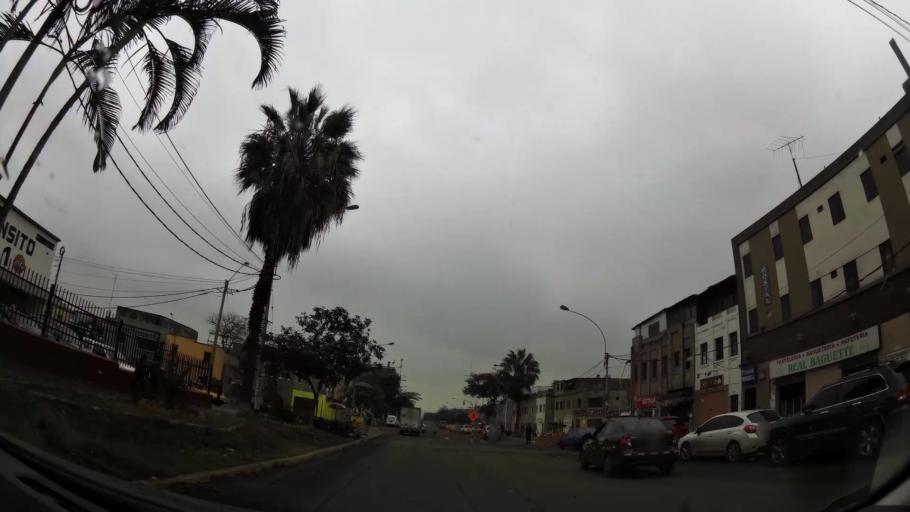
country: PE
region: Lima
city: Lima
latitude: -12.0620
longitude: -77.0203
